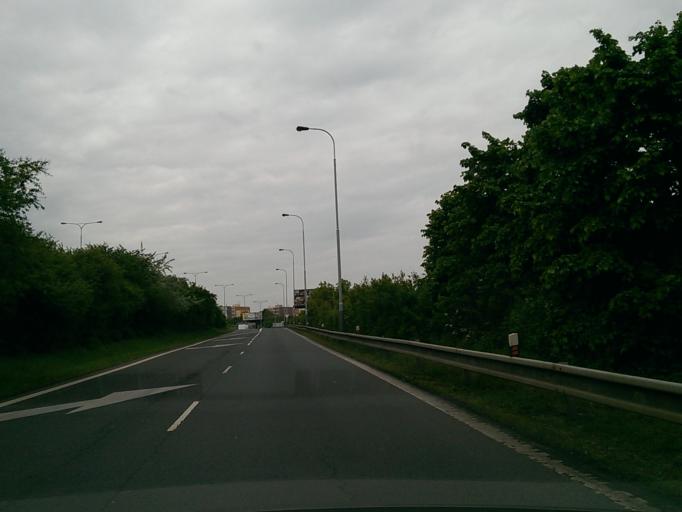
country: CZ
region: Praha
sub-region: Praha 8
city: Liben
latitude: 50.0612
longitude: 14.4936
